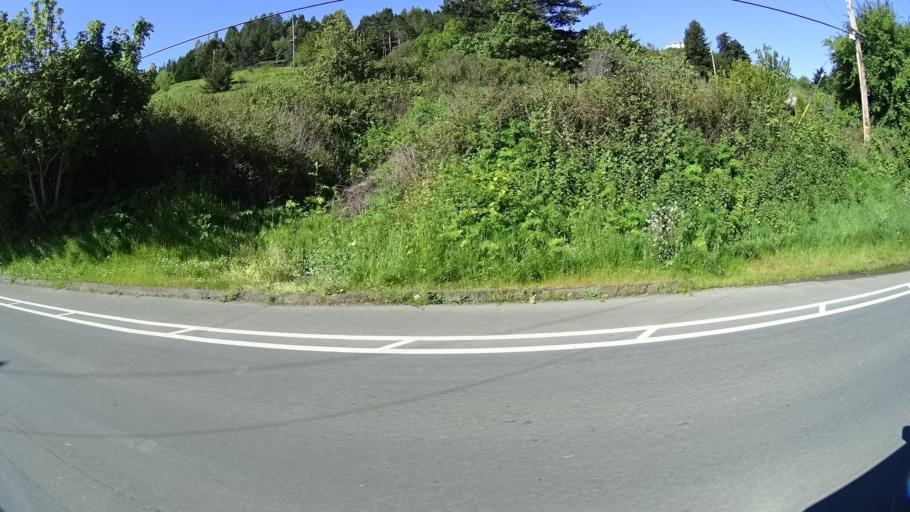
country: US
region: California
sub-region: Humboldt County
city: Rio Dell
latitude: 40.5046
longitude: -124.1110
